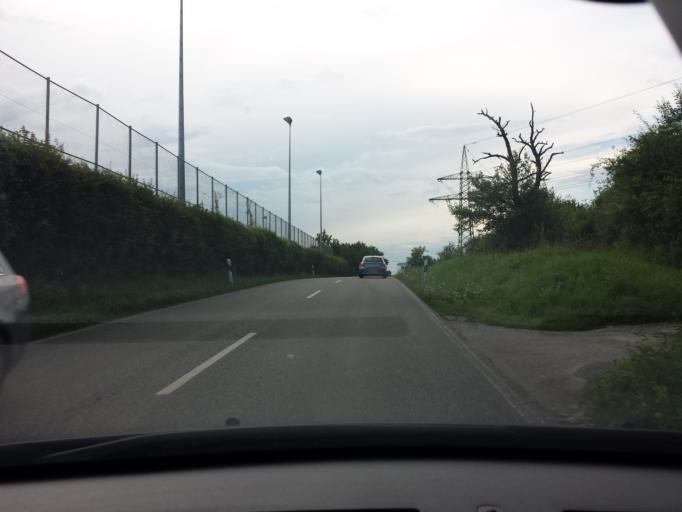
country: DE
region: Baden-Wuerttemberg
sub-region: Regierungsbezirk Stuttgart
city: Stuttgart Muehlhausen
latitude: 48.8526
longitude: 9.2674
